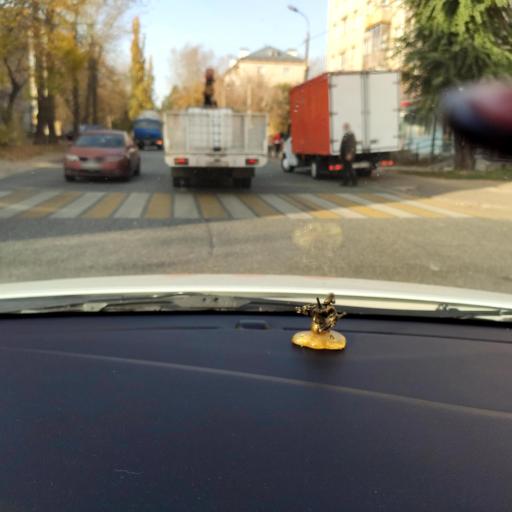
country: RU
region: Tatarstan
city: Osinovo
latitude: 55.8198
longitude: 48.8864
